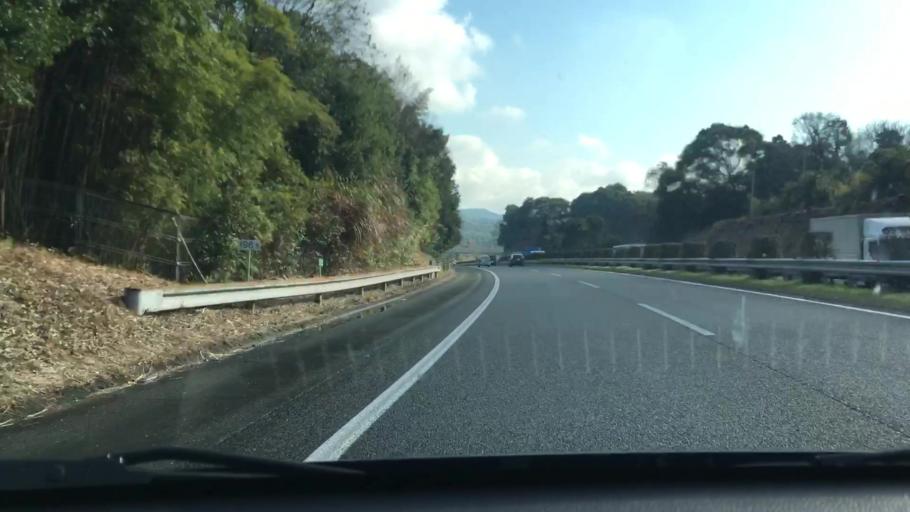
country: JP
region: Kumamoto
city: Matsubase
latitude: 32.6404
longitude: 130.7073
